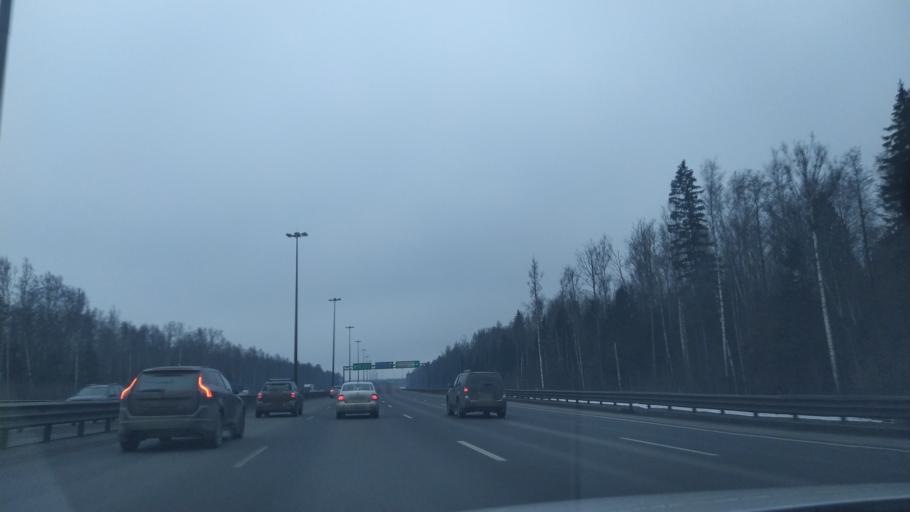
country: RU
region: Leningrad
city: Yanino Vtoroye
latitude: 59.9574
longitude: 30.5515
